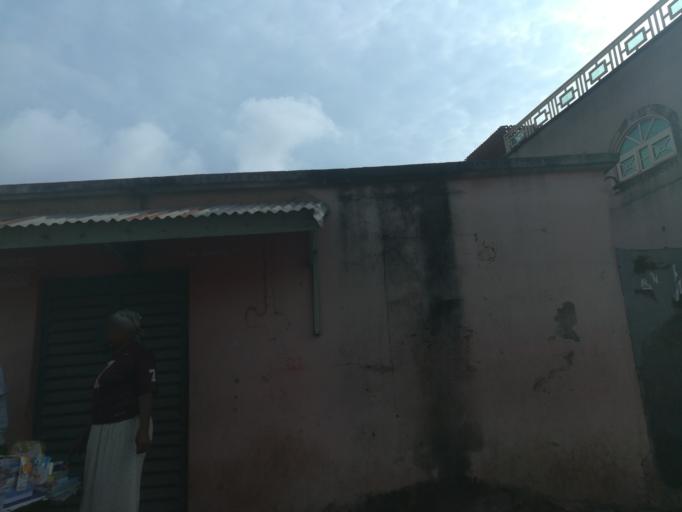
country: NG
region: Lagos
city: Agege
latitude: 6.6163
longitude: 3.3195
